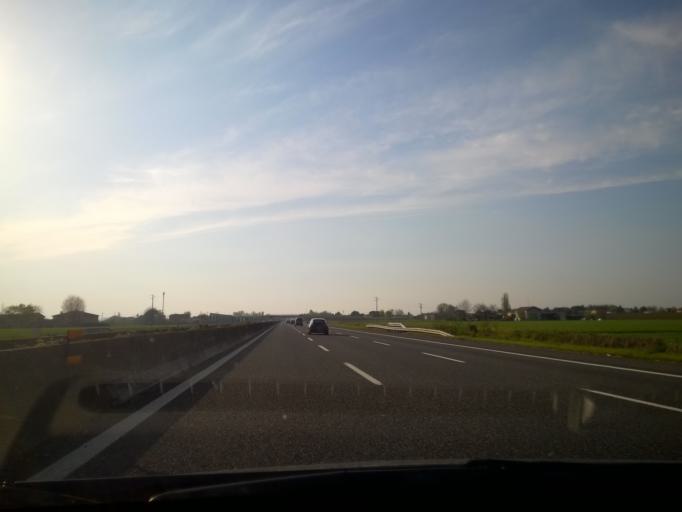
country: IT
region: Emilia-Romagna
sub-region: Provincia di Ravenna
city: Granarolo
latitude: 44.2955
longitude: 11.9756
